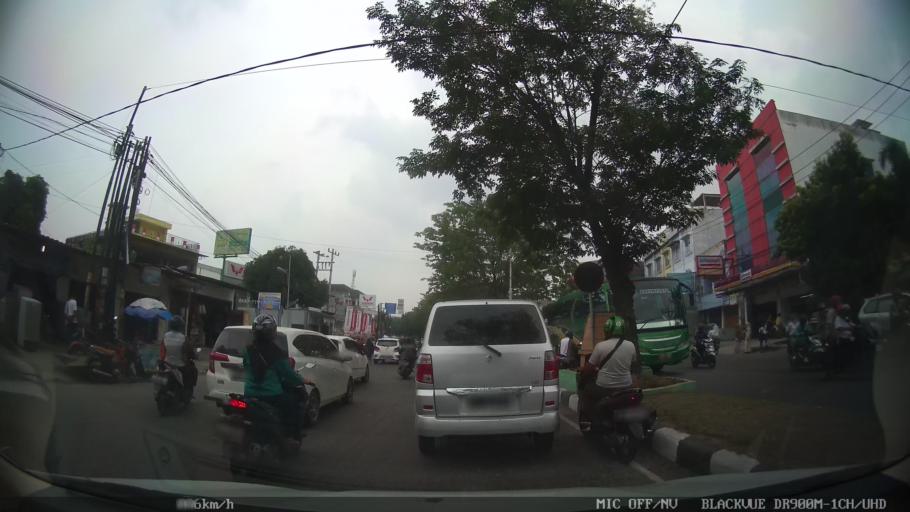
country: ID
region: North Sumatra
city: Deli Tua
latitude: 3.5492
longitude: 98.6987
